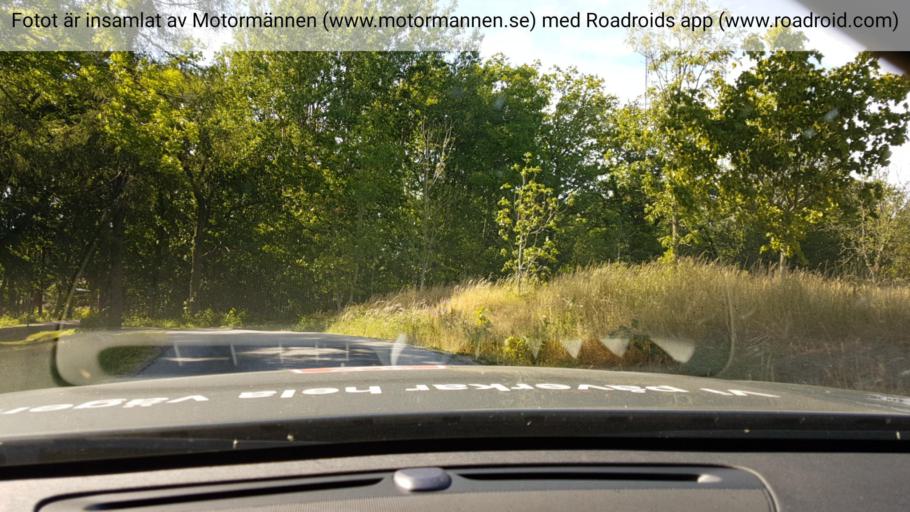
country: SE
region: Stockholm
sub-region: Haninge Kommun
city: Jordbro
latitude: 59.0079
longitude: 18.1228
